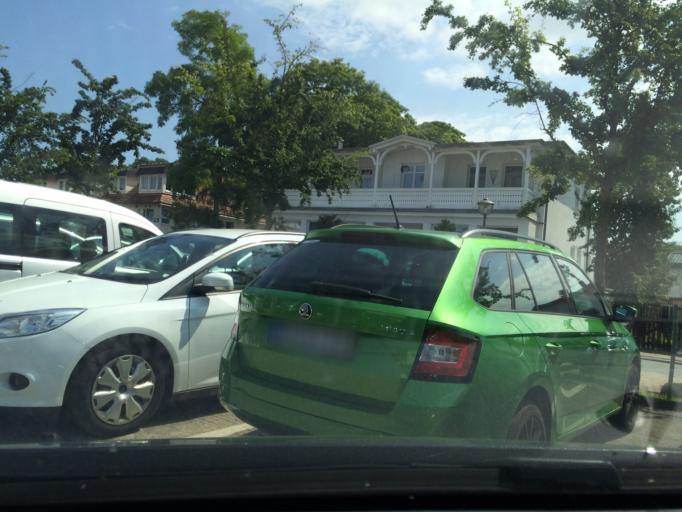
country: DE
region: Mecklenburg-Vorpommern
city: Ostseebad Binz
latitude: 54.4005
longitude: 13.6067
